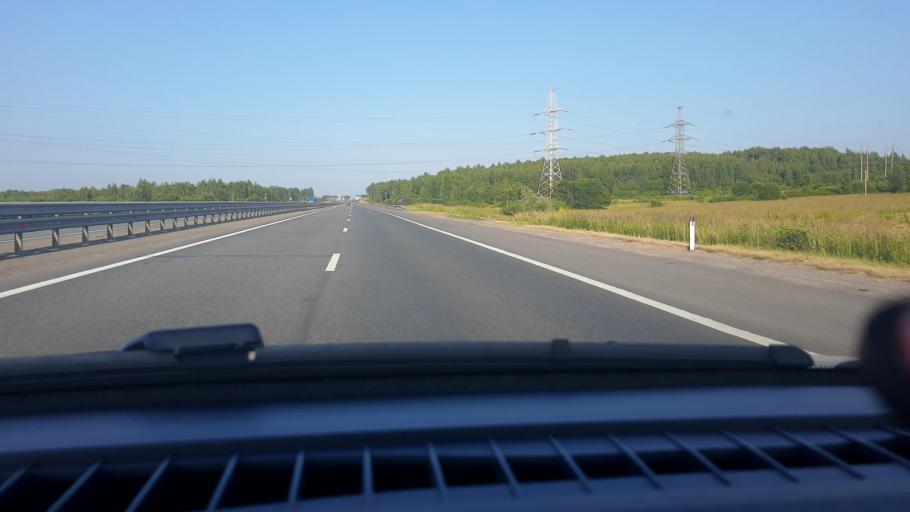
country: RU
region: Nizjnij Novgorod
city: Burevestnik
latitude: 56.1142
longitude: 43.8772
